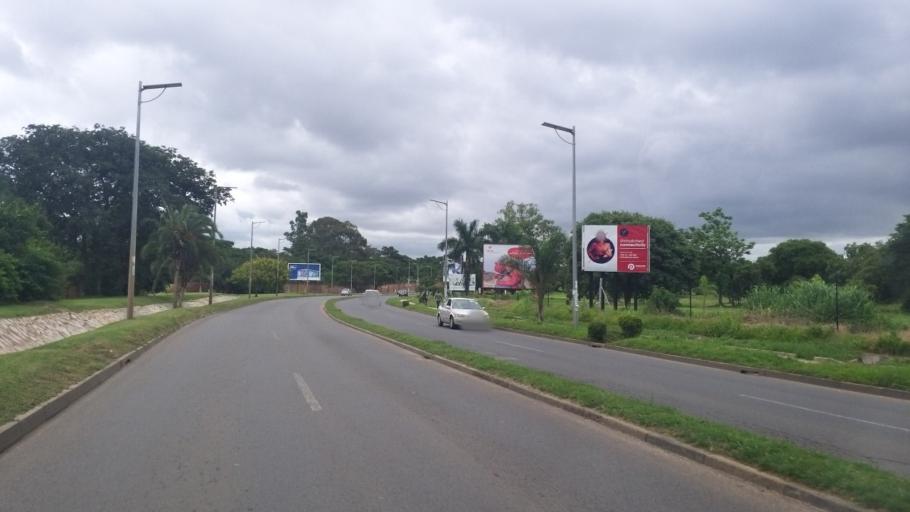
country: ZM
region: Lusaka
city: Lusaka
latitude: -15.4241
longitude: 28.3295
